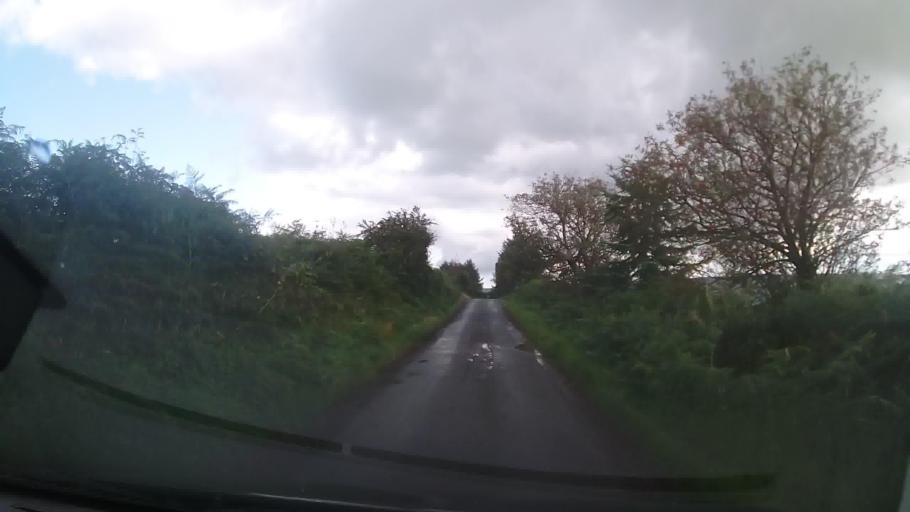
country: GB
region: England
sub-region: Shropshire
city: Norbury
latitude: 52.5723
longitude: -2.9376
